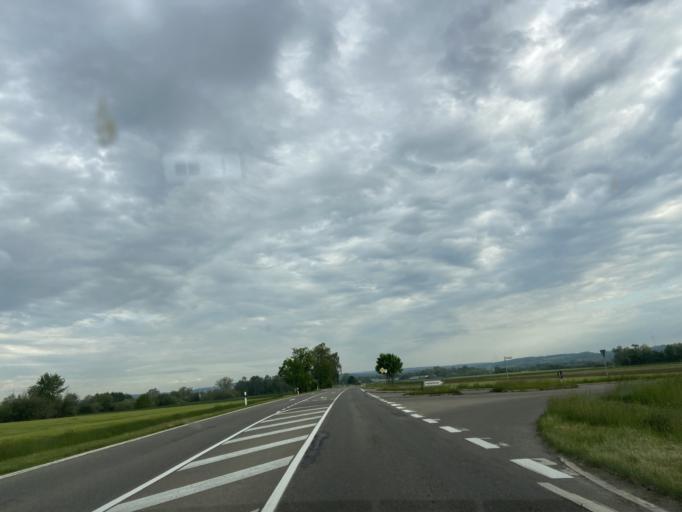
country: DE
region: Baden-Wuerttemberg
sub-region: Tuebingen Region
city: Hohentengen
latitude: 48.0415
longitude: 9.3633
